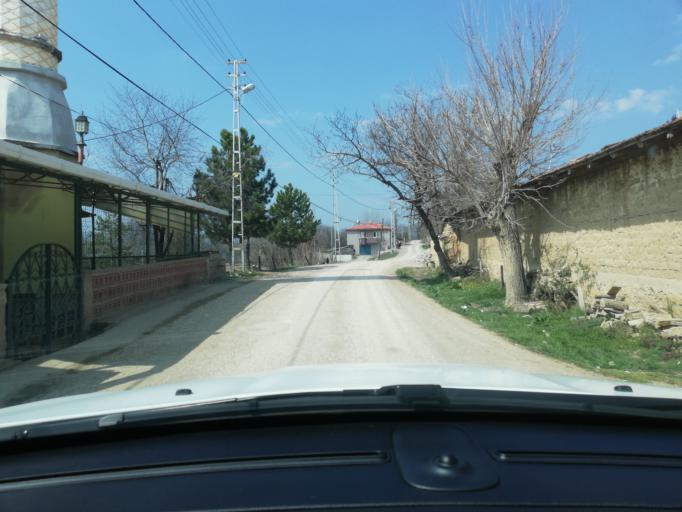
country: TR
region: Kastamonu
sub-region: Cide
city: Kastamonu
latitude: 41.4585
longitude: 33.7605
